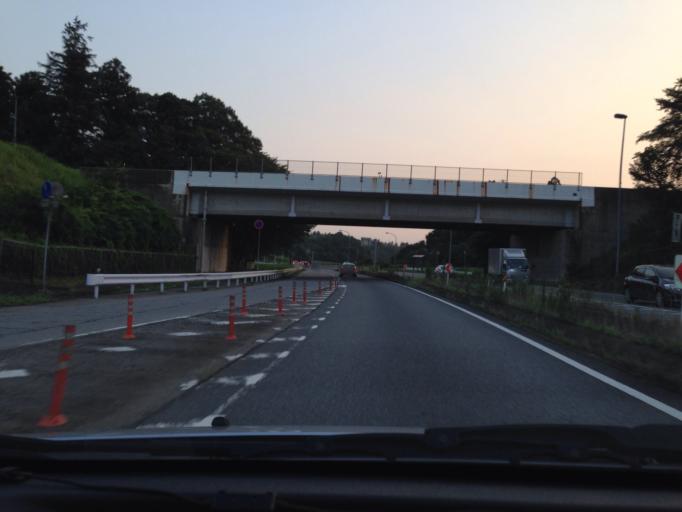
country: JP
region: Ibaraki
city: Ishioka
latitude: 36.1708
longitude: 140.2515
